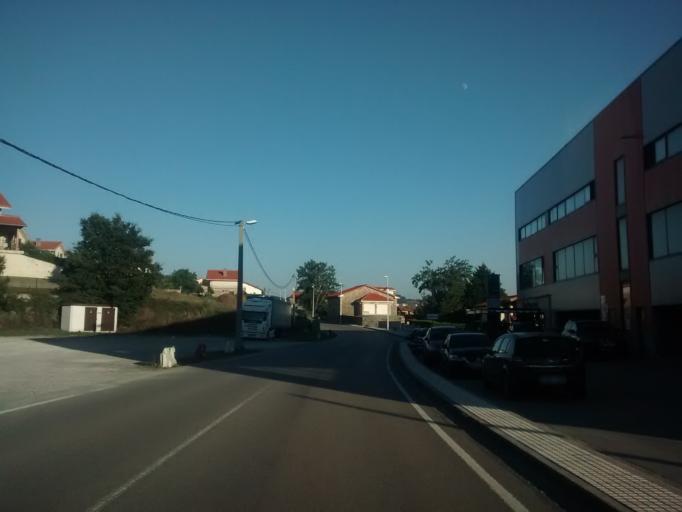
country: ES
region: Cantabria
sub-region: Provincia de Cantabria
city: San Miguel de Meruelo
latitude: 43.4604
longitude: -3.5842
